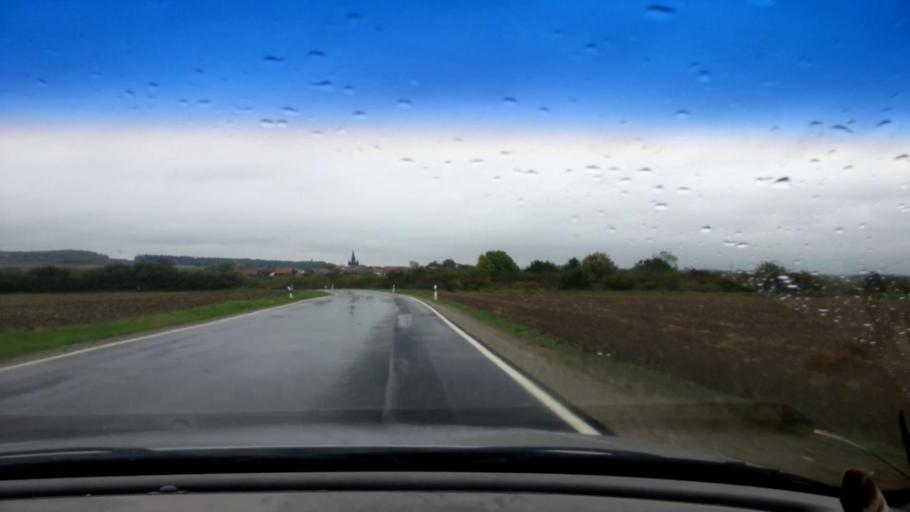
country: DE
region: Bavaria
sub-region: Upper Franconia
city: Poxdorf
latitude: 49.9454
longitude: 11.0839
